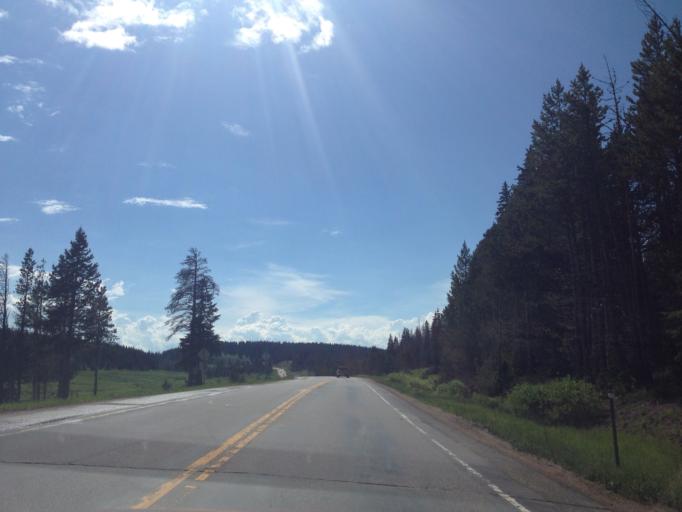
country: US
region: Colorado
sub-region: Routt County
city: Steamboat Springs
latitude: 40.3889
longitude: -106.6603
